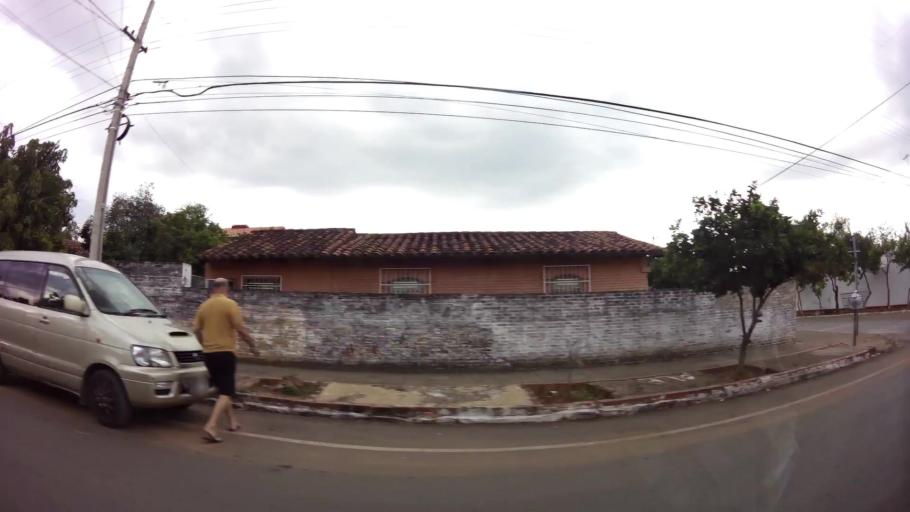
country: PY
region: Central
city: Fernando de la Mora
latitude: -25.3303
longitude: -57.5549
